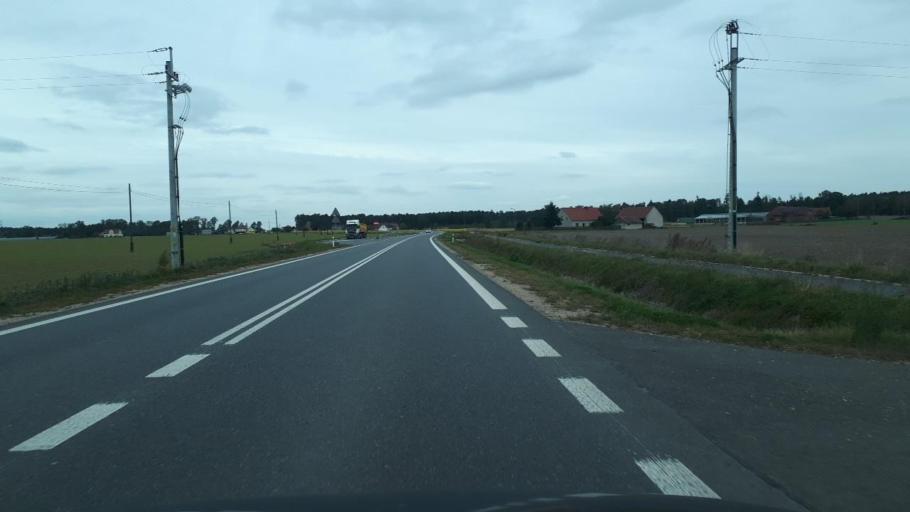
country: PL
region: Opole Voivodeship
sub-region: Powiat oleski
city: Dobrodzien
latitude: 50.6943
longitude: 18.4572
